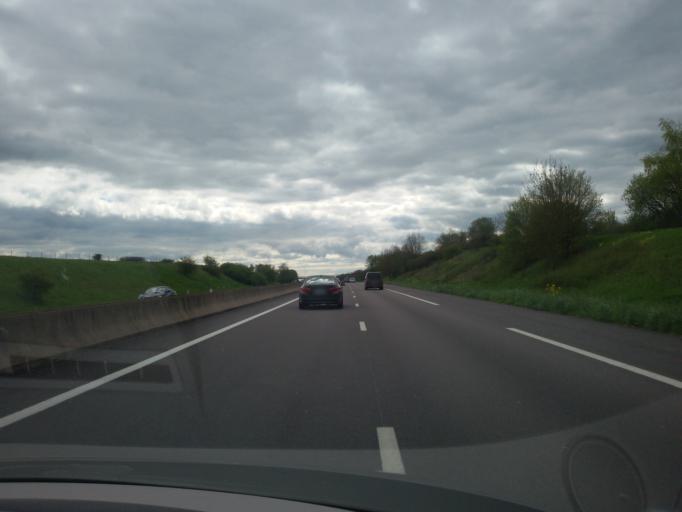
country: FR
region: Bourgogne
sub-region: Departement de la Cote-d'Or
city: Semur-en-Auxois
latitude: 47.3786
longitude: 4.3816
